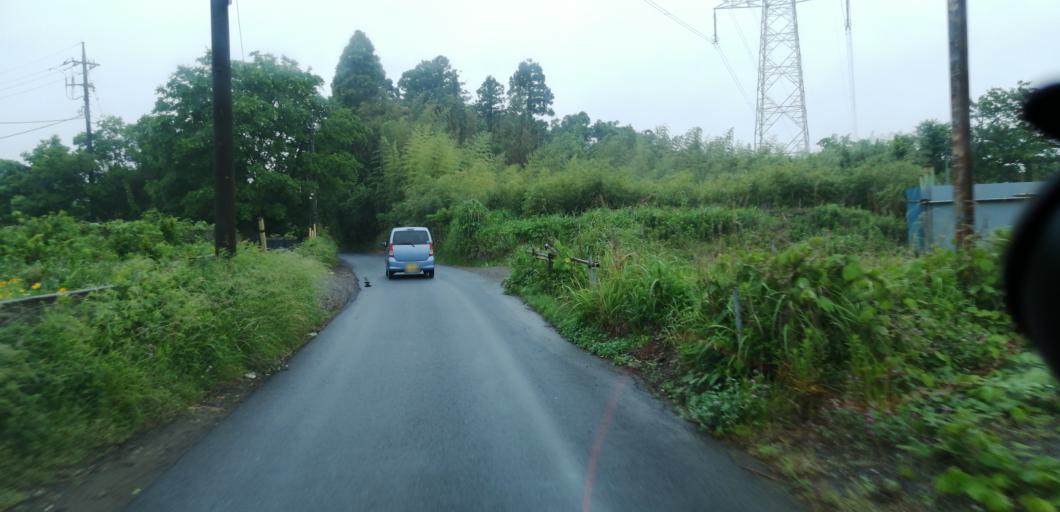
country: JP
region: Chiba
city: Ichihara
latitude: 35.4833
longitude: 140.1470
